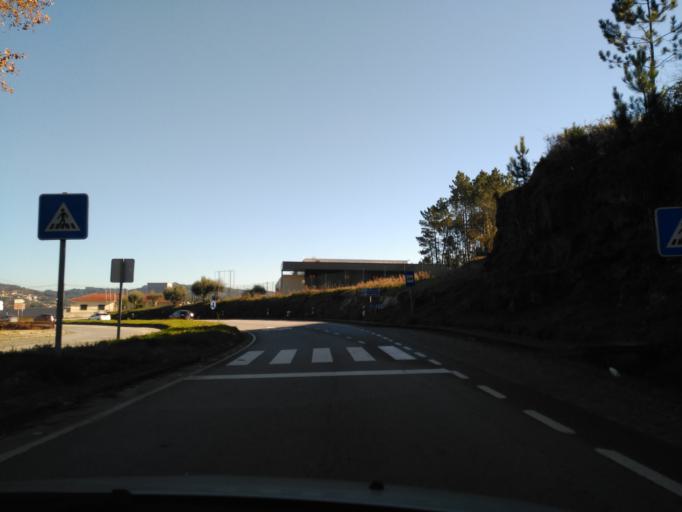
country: PT
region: Braga
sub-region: Povoa de Lanhoso
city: Povoa de Lanhoso
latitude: 41.5951
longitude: -8.2827
